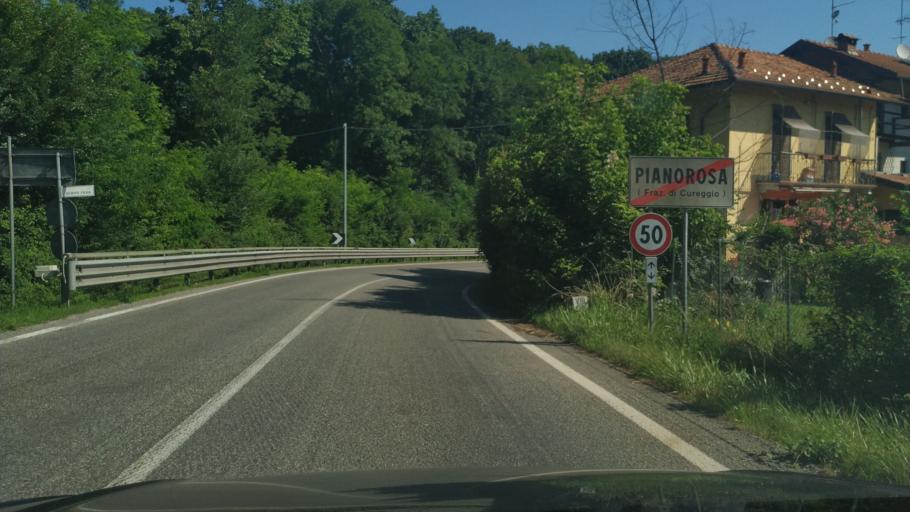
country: IT
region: Piedmont
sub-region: Provincia di Novara
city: Cureggio
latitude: 45.6687
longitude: 8.4451
